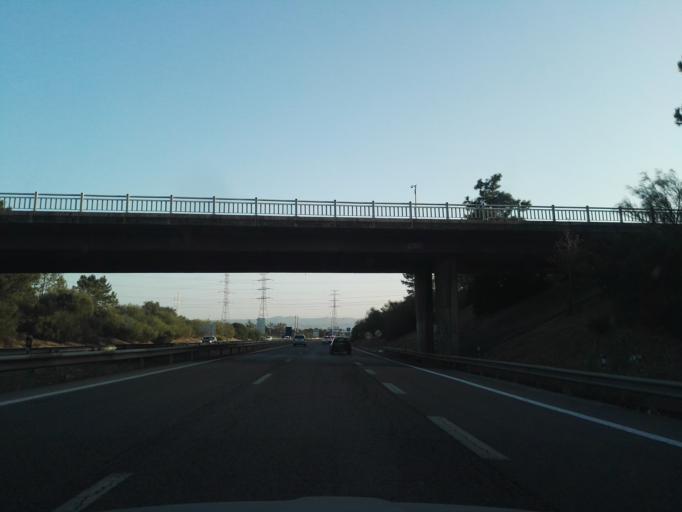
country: PT
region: Setubal
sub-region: Barreiro
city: Santo Antonio da Charneca
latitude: 38.5885
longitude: -9.0191
